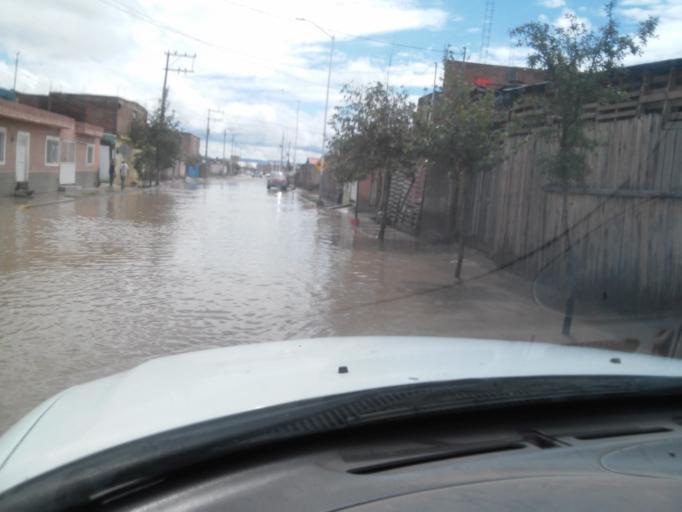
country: MX
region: Durango
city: Victoria de Durango
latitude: 24.0176
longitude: -104.6086
